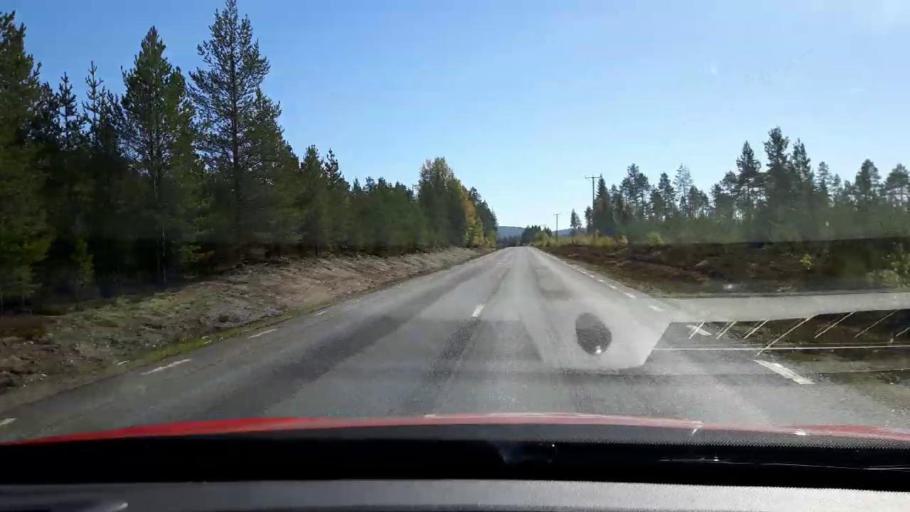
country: SE
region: Jaemtland
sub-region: Harjedalens Kommun
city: Sveg
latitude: 62.3054
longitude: 14.0517
